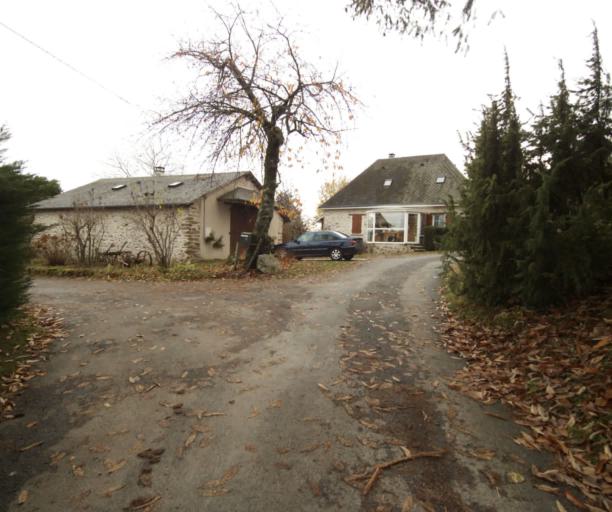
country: FR
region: Limousin
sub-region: Departement de la Correze
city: Sainte-Fortunade
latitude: 45.1838
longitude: 1.7672
